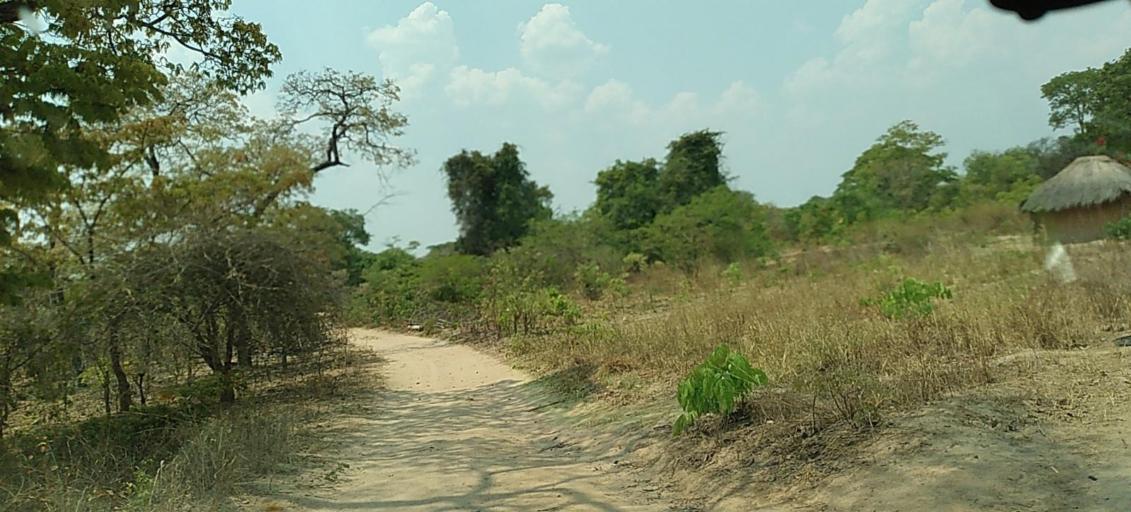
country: ZM
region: North-Western
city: Kabompo
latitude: -13.6543
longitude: 24.3735
